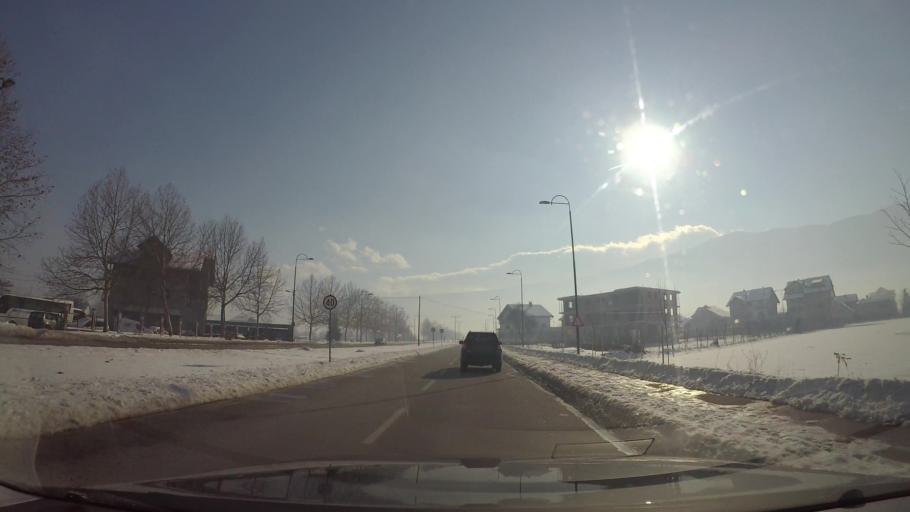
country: BA
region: Federation of Bosnia and Herzegovina
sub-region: Kanton Sarajevo
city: Sarajevo
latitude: 43.8124
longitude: 18.3094
